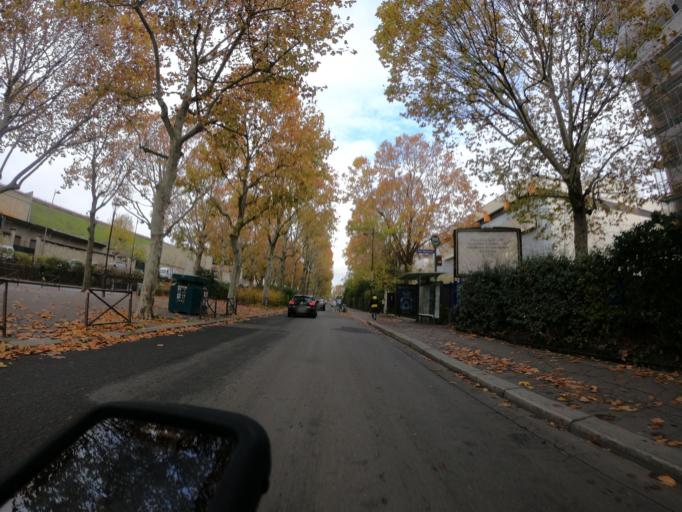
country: FR
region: Ile-de-France
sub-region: Departement du Val-de-Marne
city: Gentilly
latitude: 48.8244
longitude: 2.3362
